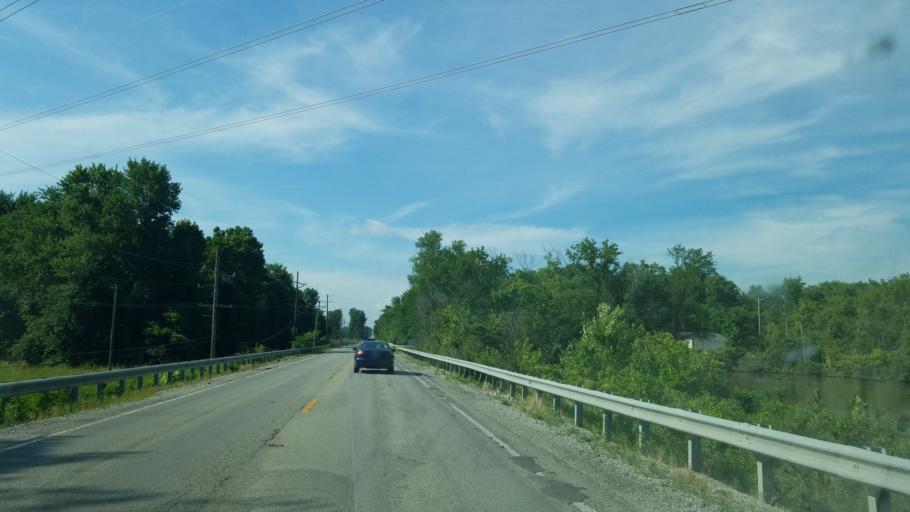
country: US
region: Illinois
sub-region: Saint Clair County
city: Lebanon
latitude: 38.5803
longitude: -89.8078
